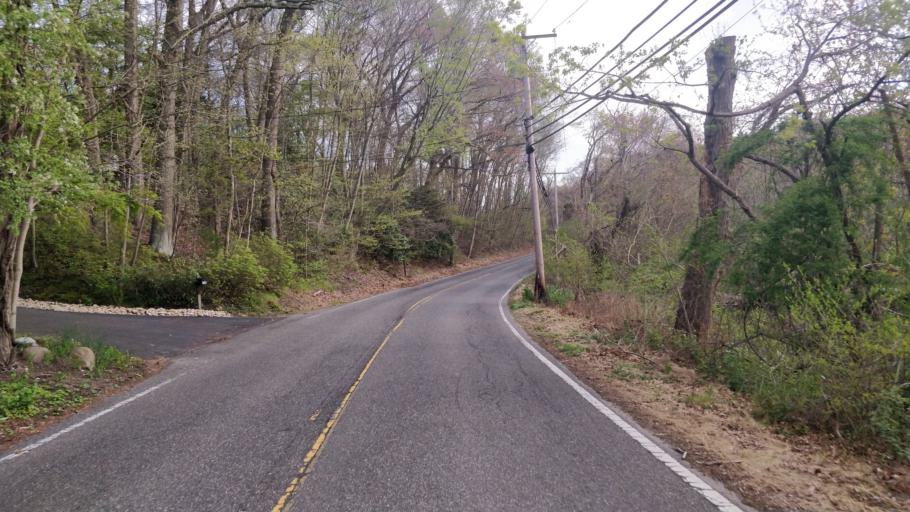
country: US
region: New York
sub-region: Suffolk County
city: Fort Salonga
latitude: 40.9162
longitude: -73.3115
